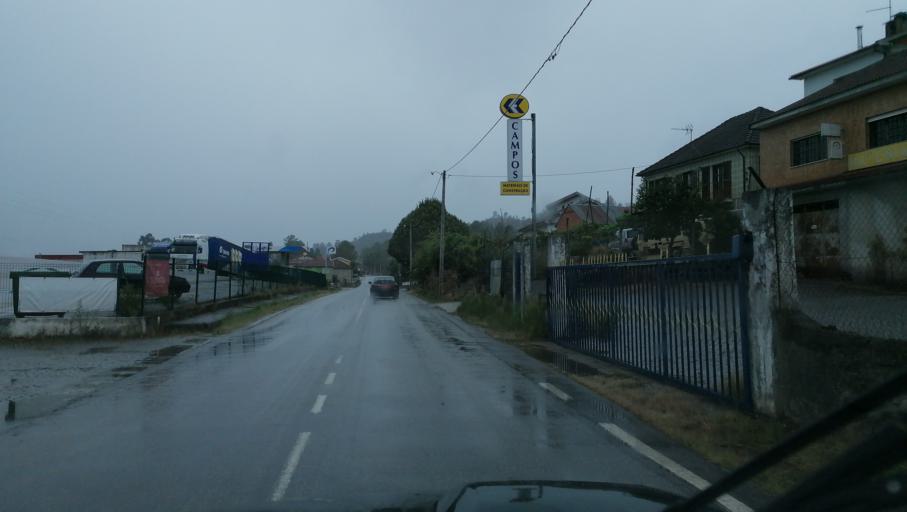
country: PT
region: Braga
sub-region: Cabeceiras de Basto
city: Cabeceiras de Basto
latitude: 41.4973
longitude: -7.9203
